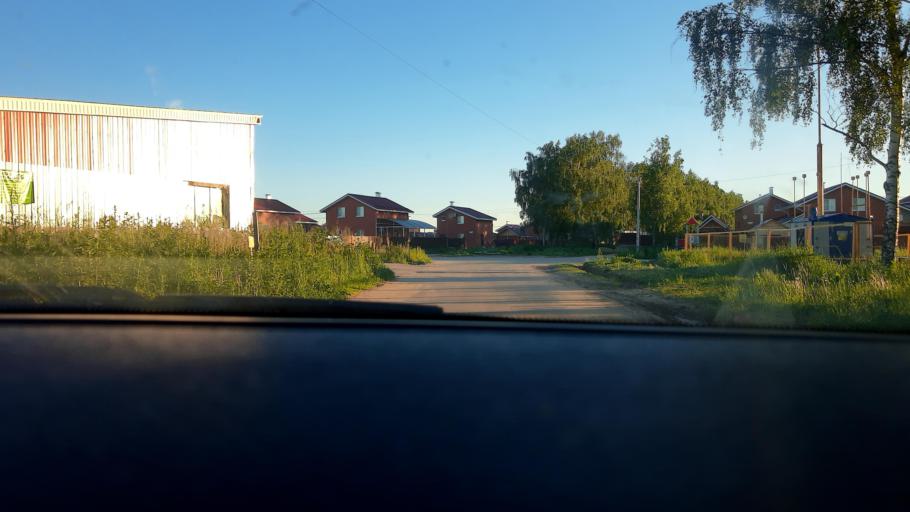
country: RU
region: Nizjnij Novgorod
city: Afonino
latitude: 56.1964
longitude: 44.0805
